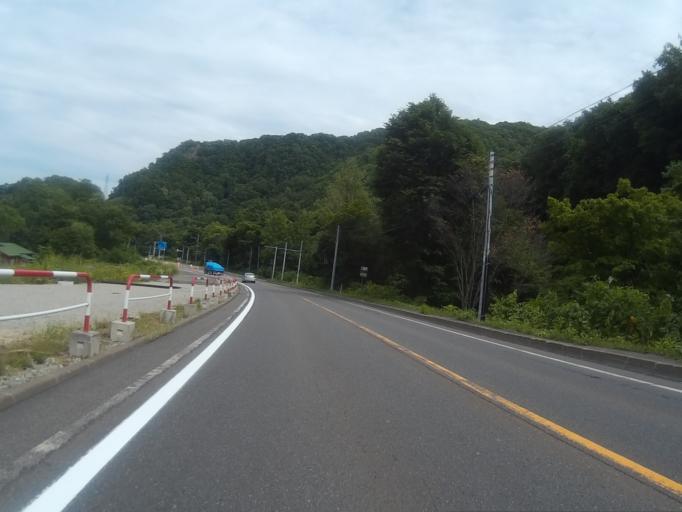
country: JP
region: Hokkaido
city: Sapporo
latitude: 42.9693
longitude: 141.1794
